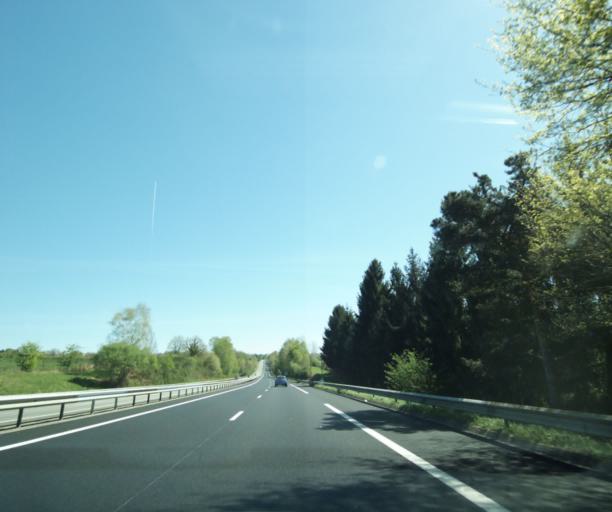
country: FR
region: Limousin
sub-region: Departement de la Haute-Vienne
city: Boisseuil
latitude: 45.7721
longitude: 1.3130
